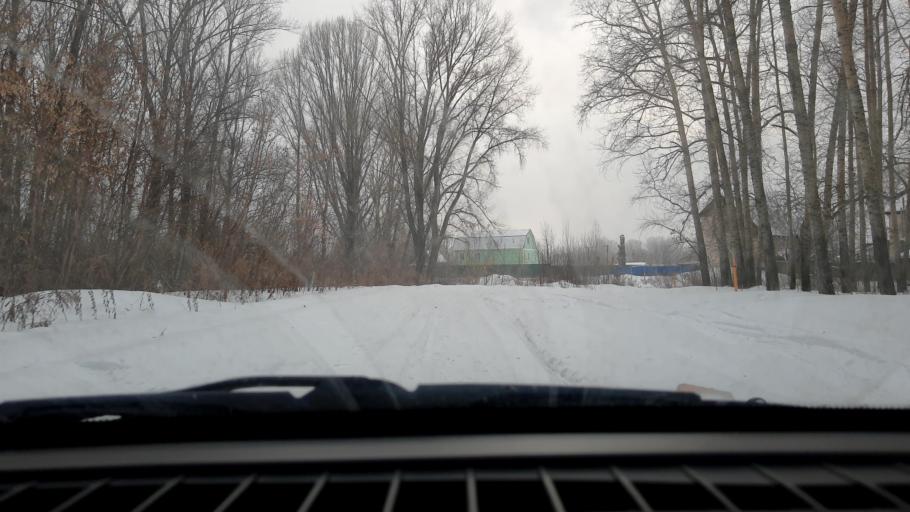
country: RU
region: Bashkortostan
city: Ufa
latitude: 54.7230
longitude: 55.9067
